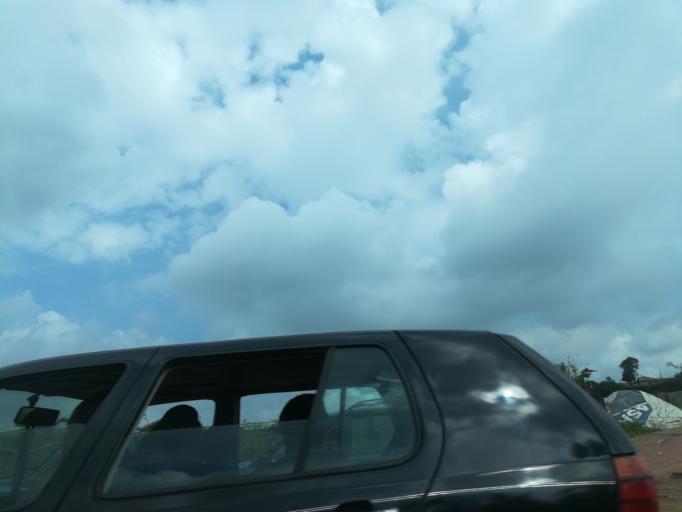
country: NG
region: Lagos
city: Ikorodu
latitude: 6.6582
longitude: 3.5848
